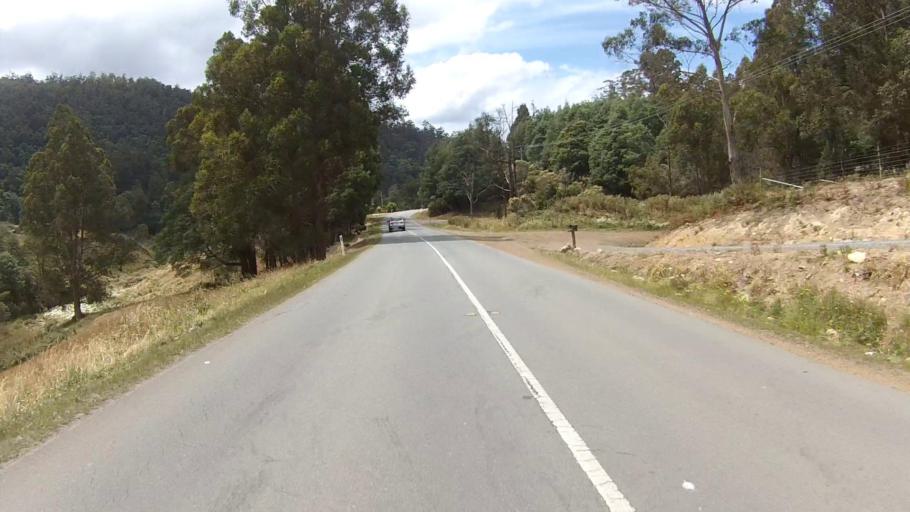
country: AU
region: Tasmania
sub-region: Kingborough
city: Kettering
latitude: -43.1044
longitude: 147.2078
